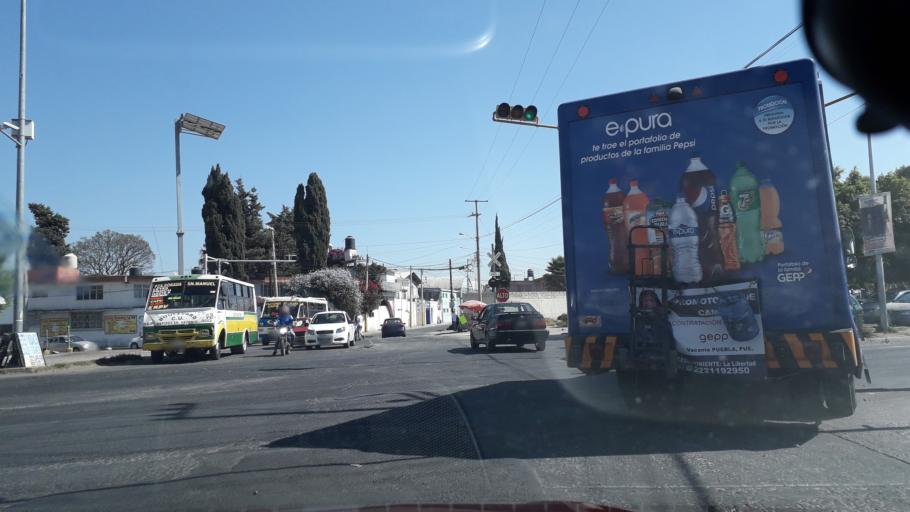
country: MX
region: Puebla
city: Puebla
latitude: 19.0808
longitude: -98.2111
